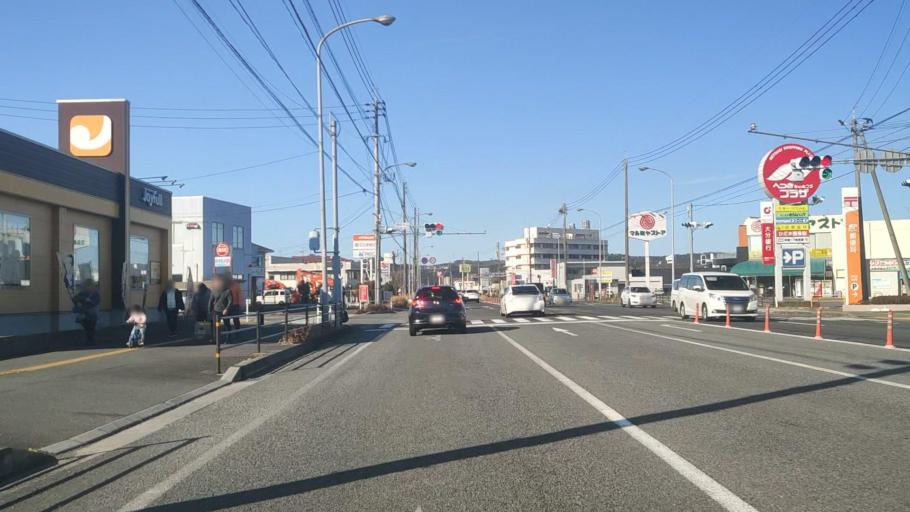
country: JP
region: Oita
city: Oita
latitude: 33.1519
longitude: 131.6565
